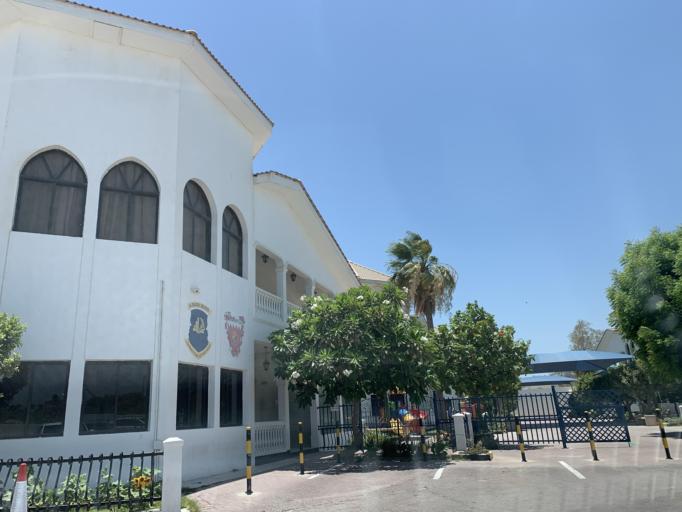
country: BH
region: Manama
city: Jidd Hafs
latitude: 26.2191
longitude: 50.4847
